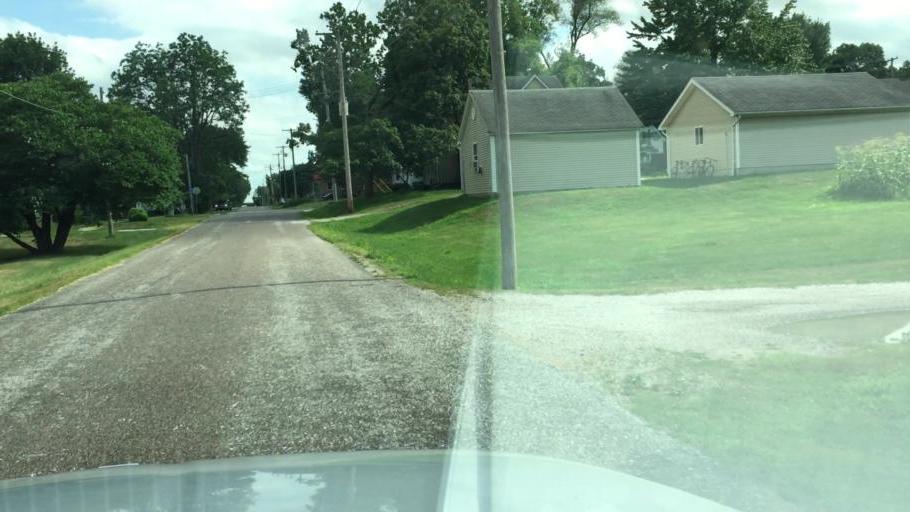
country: US
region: Illinois
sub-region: Hancock County
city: Carthage
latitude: 40.4143
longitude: -91.1275
